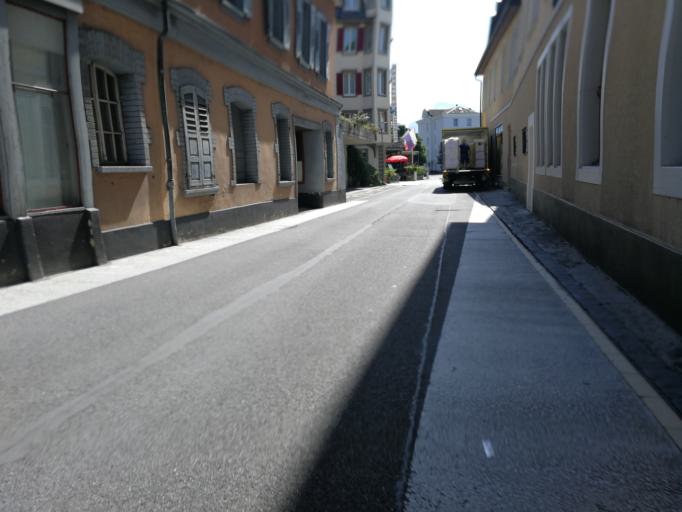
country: CH
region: Lucerne
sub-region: Lucerne-Land District
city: Weggis
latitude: 47.0322
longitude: 8.4365
